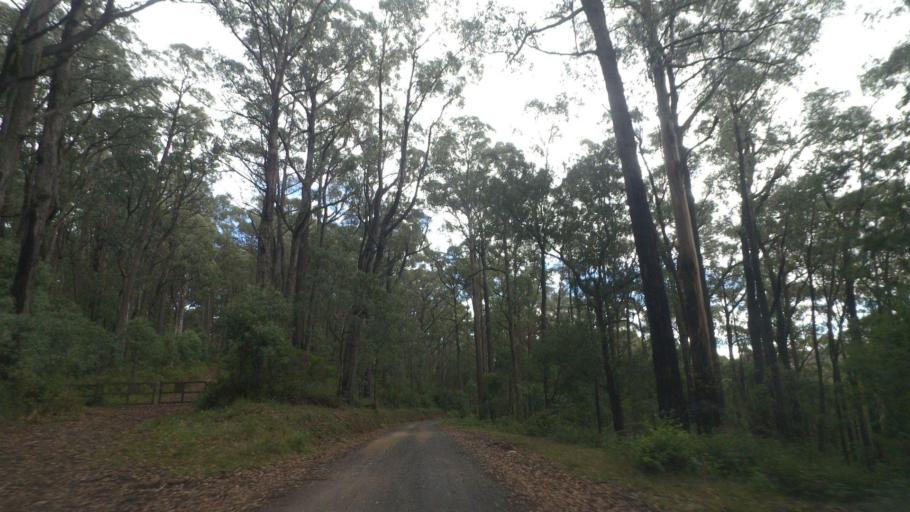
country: AU
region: Victoria
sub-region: Cardinia
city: Gembrook
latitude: -37.8946
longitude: 145.6568
